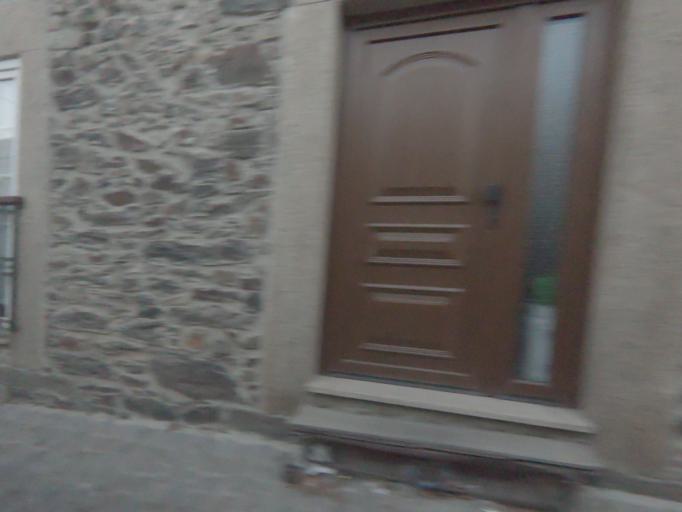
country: PT
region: Vila Real
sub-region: Peso da Regua
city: Peso da Regua
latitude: 41.1777
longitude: -7.7267
